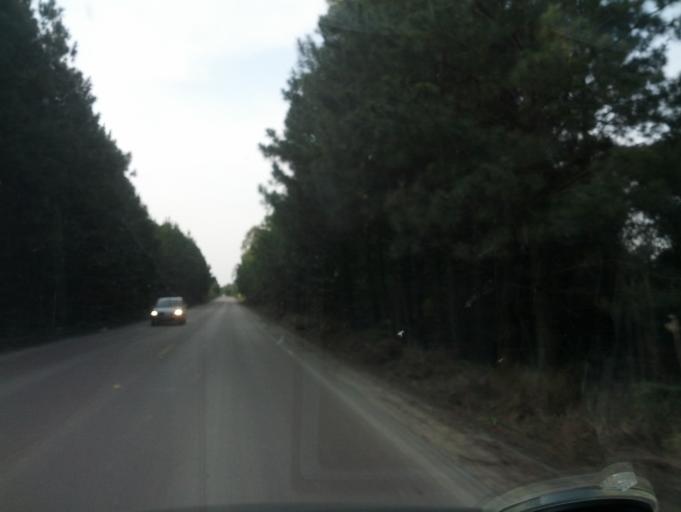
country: BR
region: Santa Catarina
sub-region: Otacilio Costa
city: Otacilio Costa
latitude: -27.4374
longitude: -50.1240
